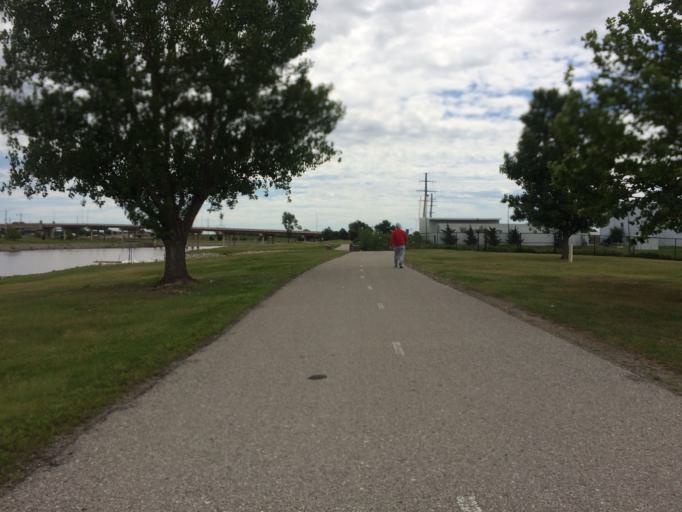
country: US
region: Oklahoma
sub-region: Oklahoma County
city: Oklahoma City
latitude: 35.4590
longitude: -97.5422
